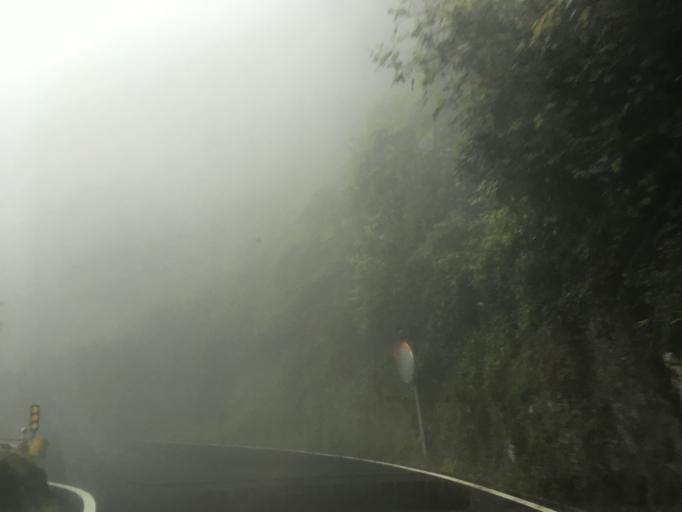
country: TW
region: Taiwan
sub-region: Hualien
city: Hualian
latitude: 24.1969
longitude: 121.4281
